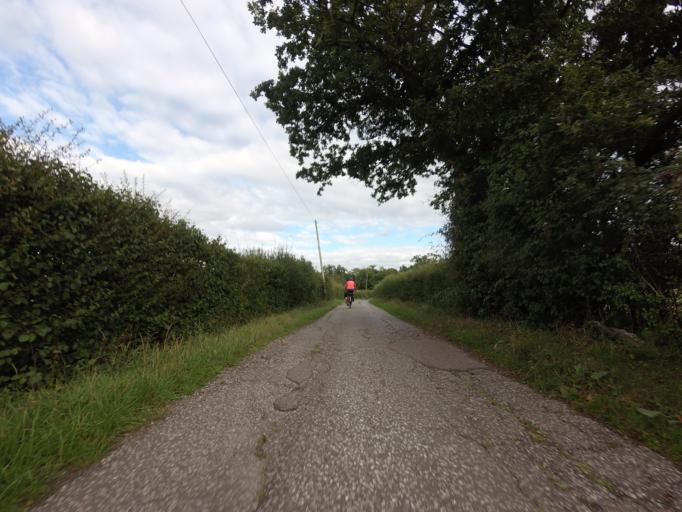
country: GB
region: England
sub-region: Kent
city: Staplehurst
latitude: 51.2106
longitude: 0.5585
